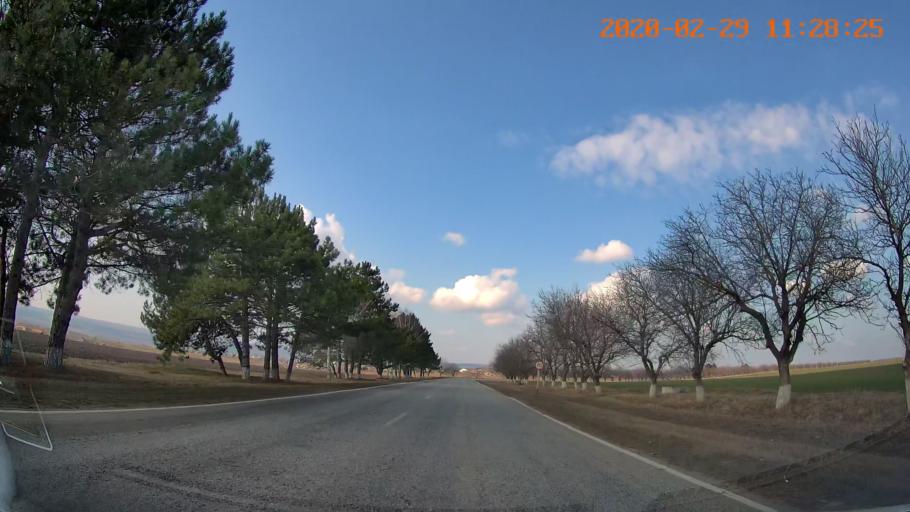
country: MD
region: Telenesti
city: Cocieri
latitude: 47.4812
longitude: 29.1358
